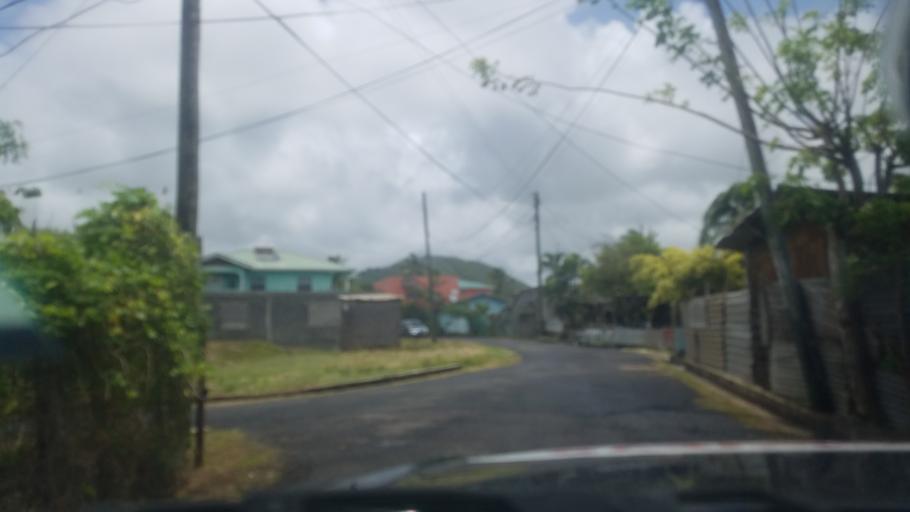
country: LC
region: Vieux-Fort
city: Vieux Fort
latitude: 13.7420
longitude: -60.9555
